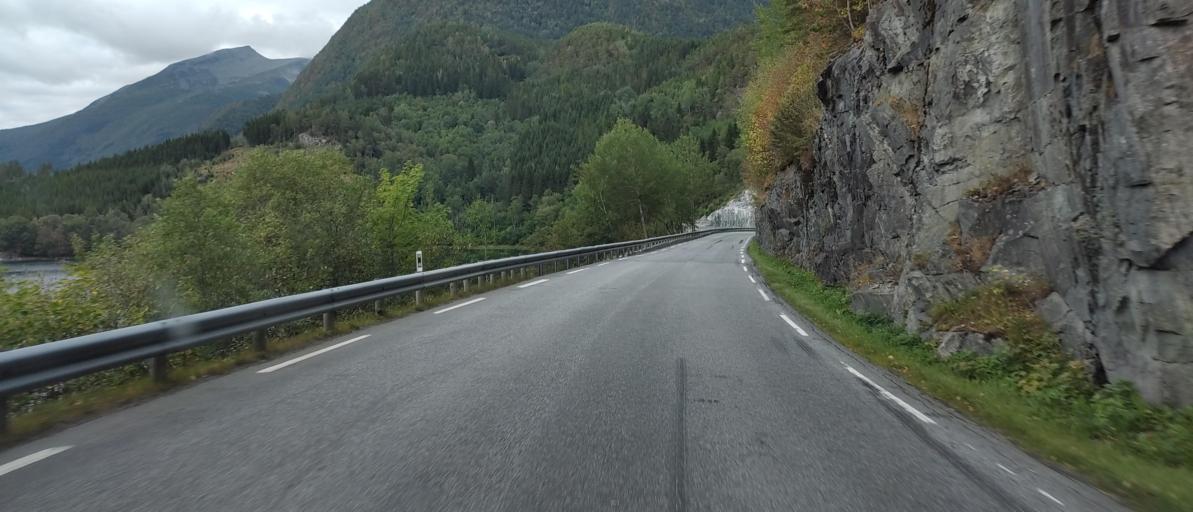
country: NO
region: More og Romsdal
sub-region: Rauma
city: Andalsnes
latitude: 62.5779
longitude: 7.5385
